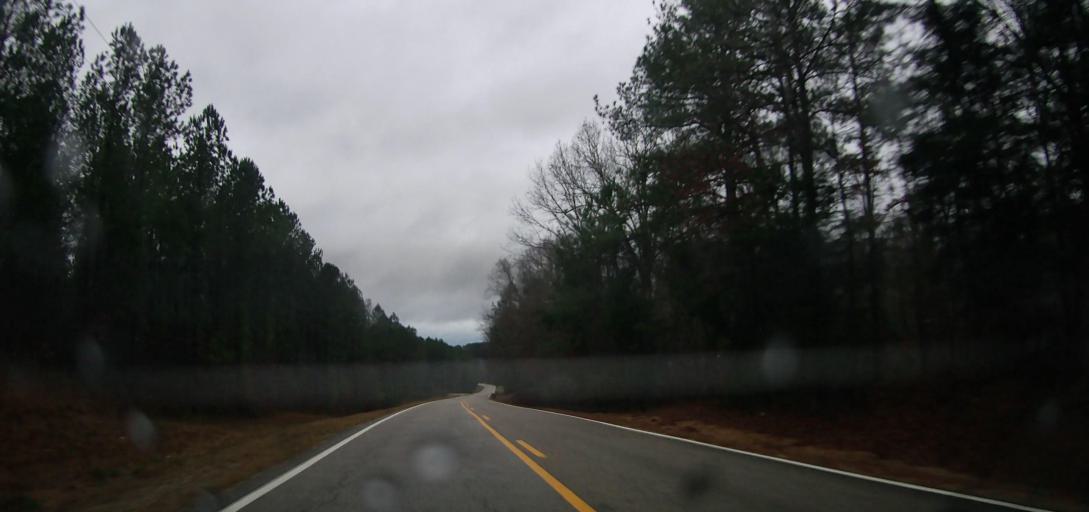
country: US
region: Alabama
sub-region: Bibb County
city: Centreville
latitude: 32.9861
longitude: -87.1470
